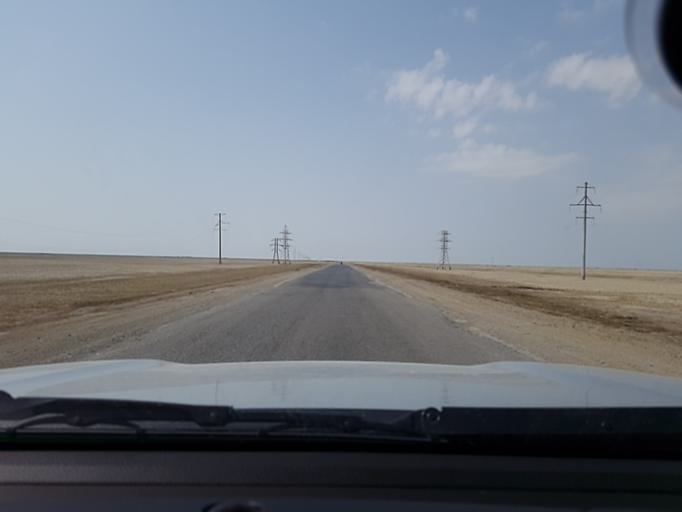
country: TM
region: Balkan
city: Gumdag
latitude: 39.0564
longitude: 54.5842
